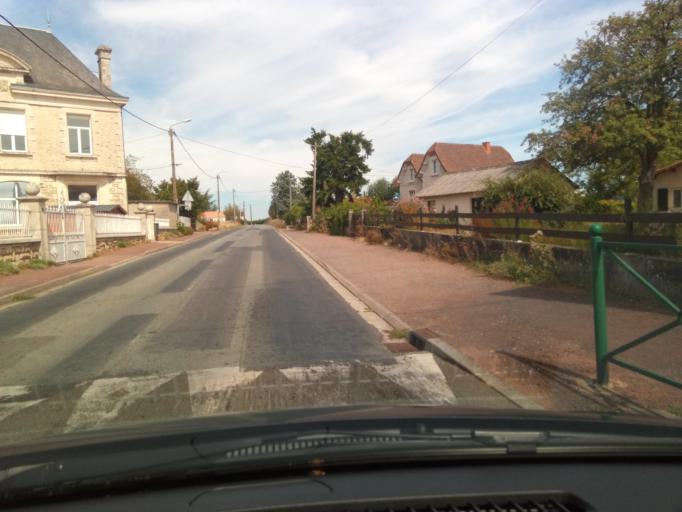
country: FR
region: Poitou-Charentes
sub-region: Departement de la Vienne
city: Terce
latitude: 46.5177
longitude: 0.5646
